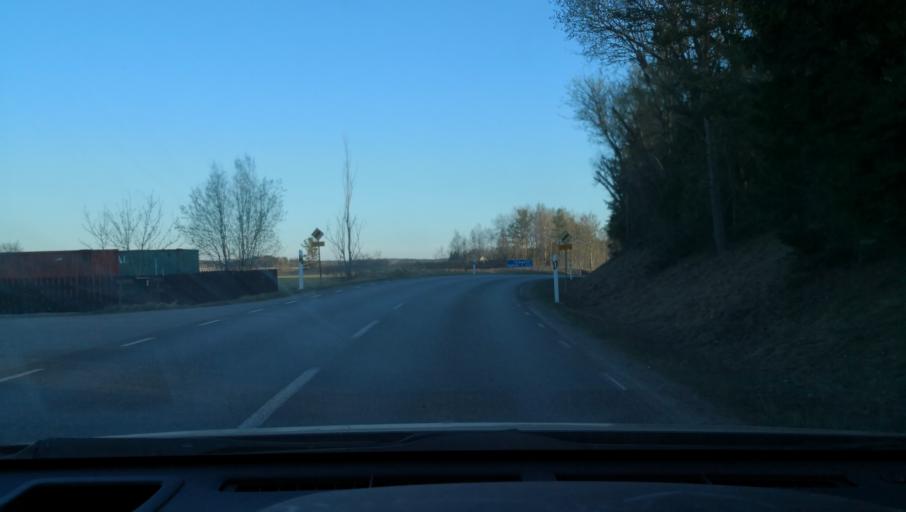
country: SE
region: Uppsala
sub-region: Enkopings Kommun
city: Irsta
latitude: 59.7718
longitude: 16.9131
